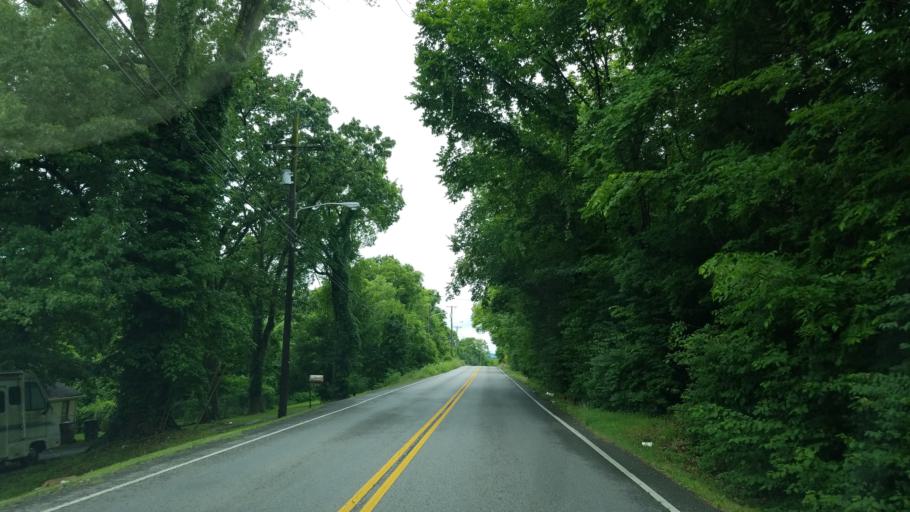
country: US
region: Tennessee
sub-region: Rutherford County
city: La Vergne
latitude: 36.0564
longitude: -86.6645
